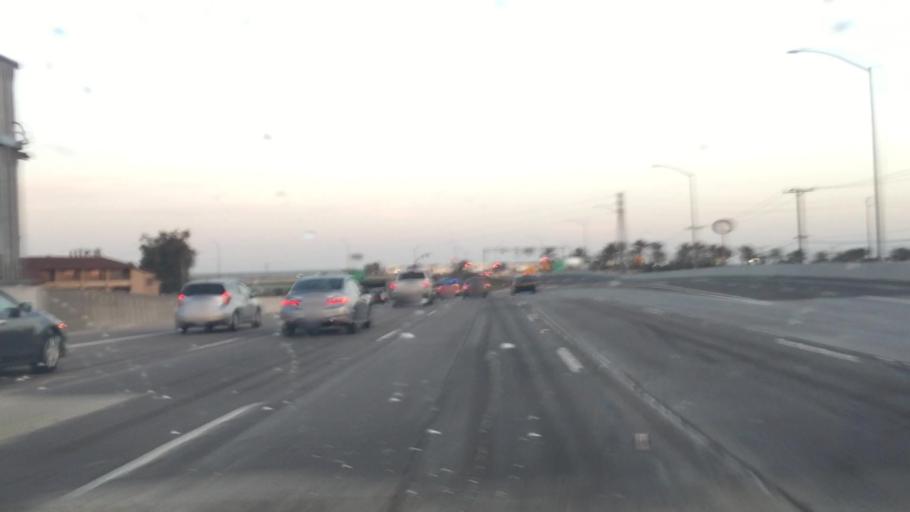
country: US
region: California
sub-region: Orange County
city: Placentia
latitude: 33.8499
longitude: -117.8355
